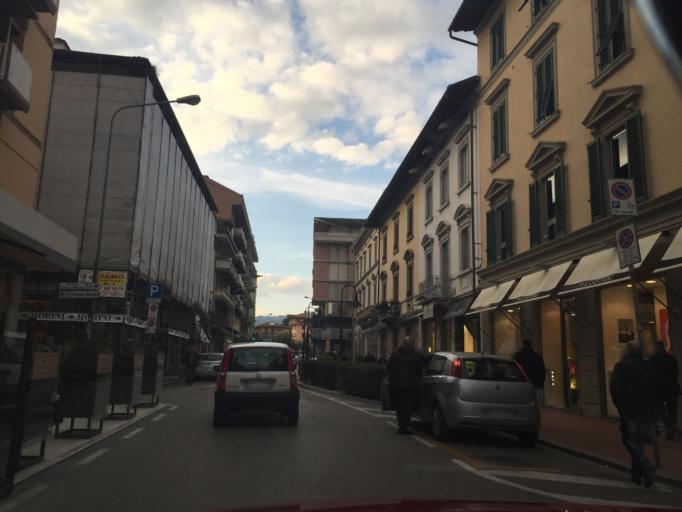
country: IT
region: Tuscany
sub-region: Provincia di Pistoia
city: Montecatini-Terme
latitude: 43.8818
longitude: 10.7732
